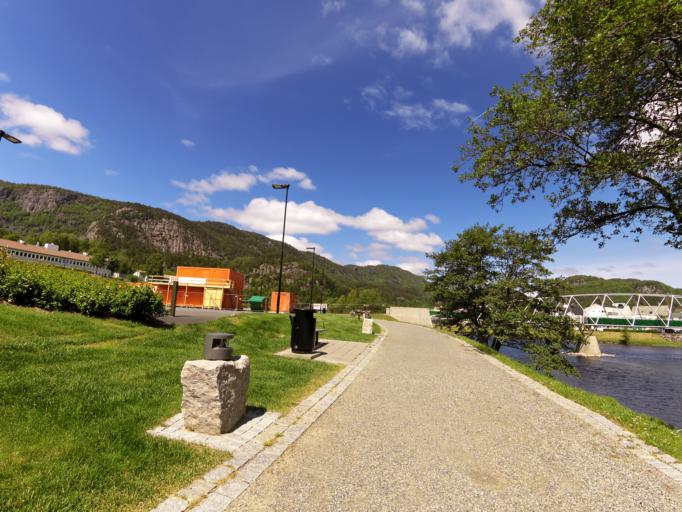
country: NO
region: Vest-Agder
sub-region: Kvinesdal
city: Liknes
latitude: 58.3146
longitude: 6.9604
